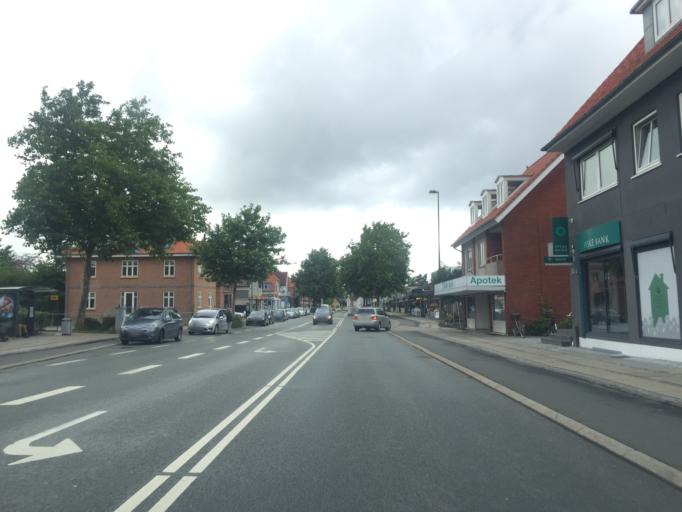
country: DK
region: South Denmark
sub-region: Odense Kommune
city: Odense
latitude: 55.3718
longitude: 10.3707
